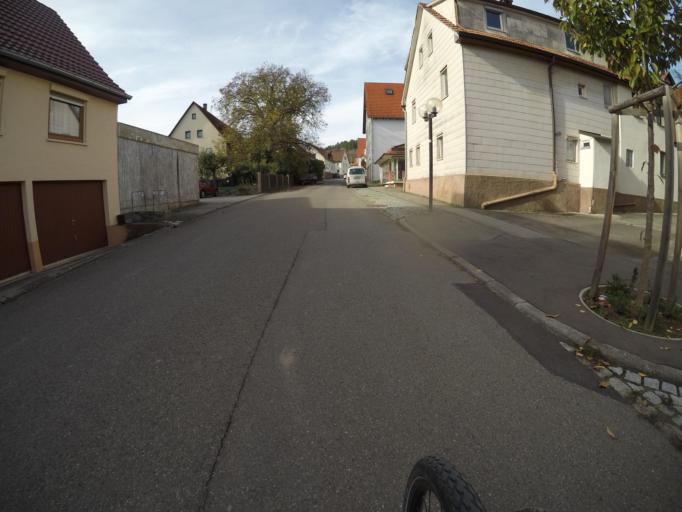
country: DE
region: Baden-Wuerttemberg
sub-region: Karlsruhe Region
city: Simmozheim
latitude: 48.7497
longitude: 8.8113
